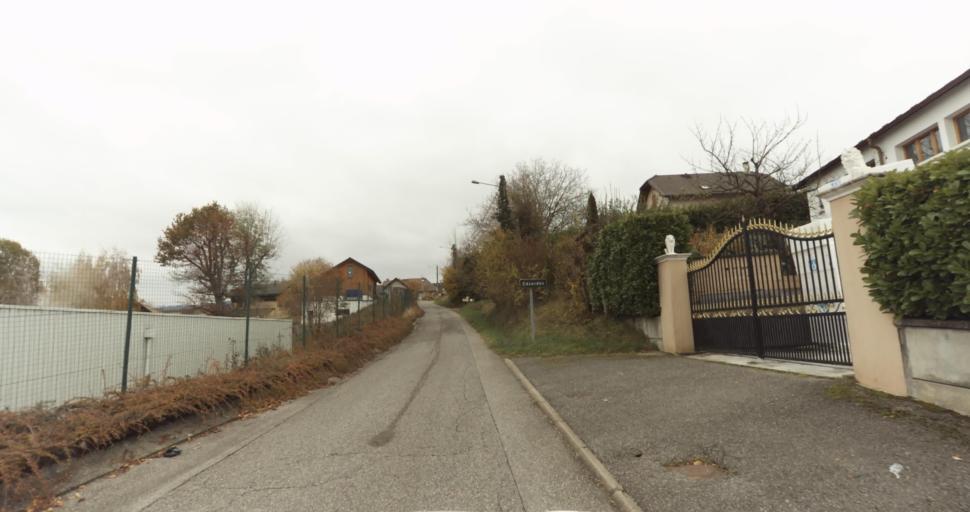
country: FR
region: Rhone-Alpes
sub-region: Departement de la Haute-Savoie
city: Seynod
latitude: 45.8874
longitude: 6.0773
